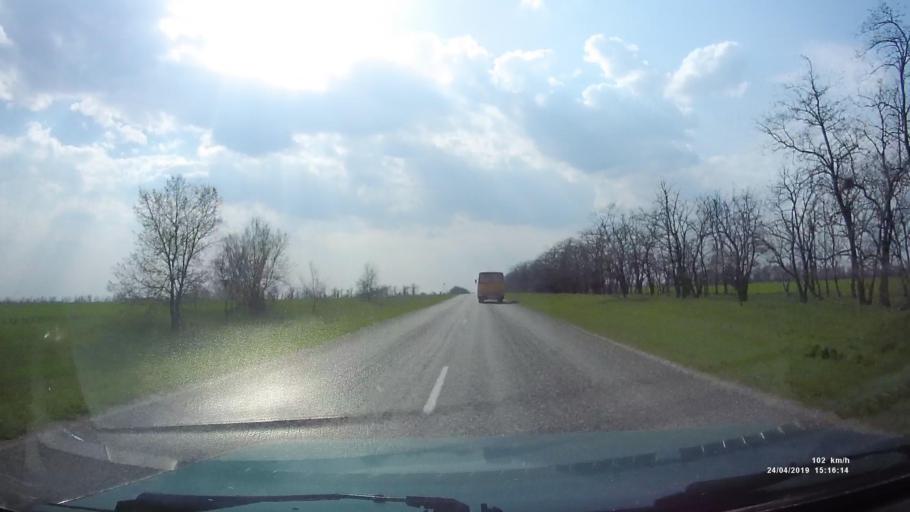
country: RU
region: Rostov
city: Remontnoye
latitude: 46.5451
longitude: 43.2189
